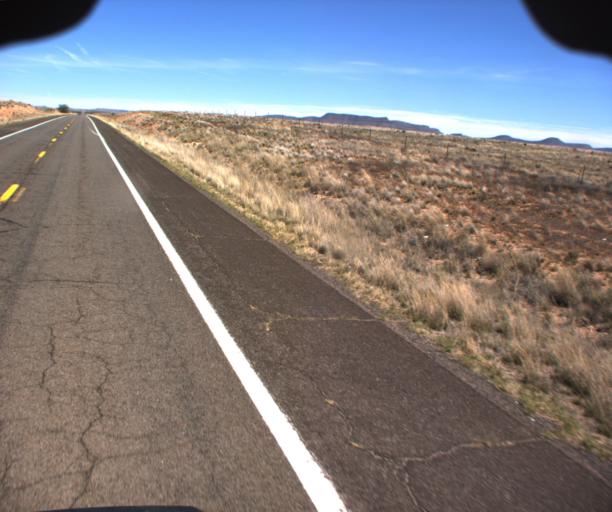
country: US
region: Arizona
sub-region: Mohave County
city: Peach Springs
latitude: 35.4718
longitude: -113.5903
